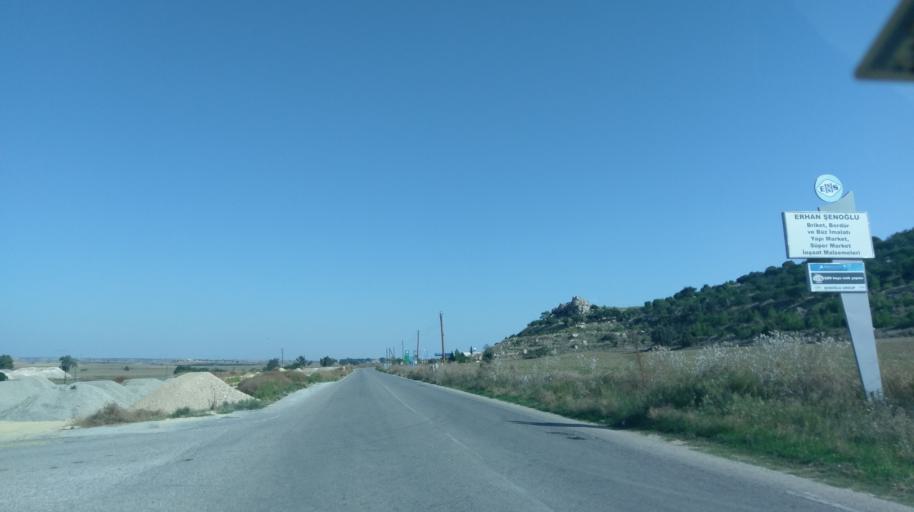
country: CY
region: Ammochostos
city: Trikomo
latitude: 35.3509
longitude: 33.9961
